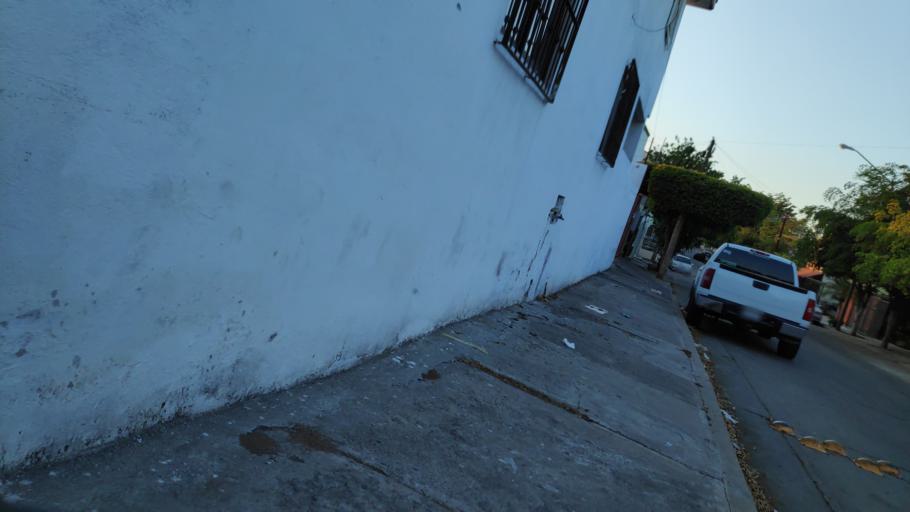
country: MX
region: Sinaloa
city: Culiacan
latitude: 24.7869
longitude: -107.4029
